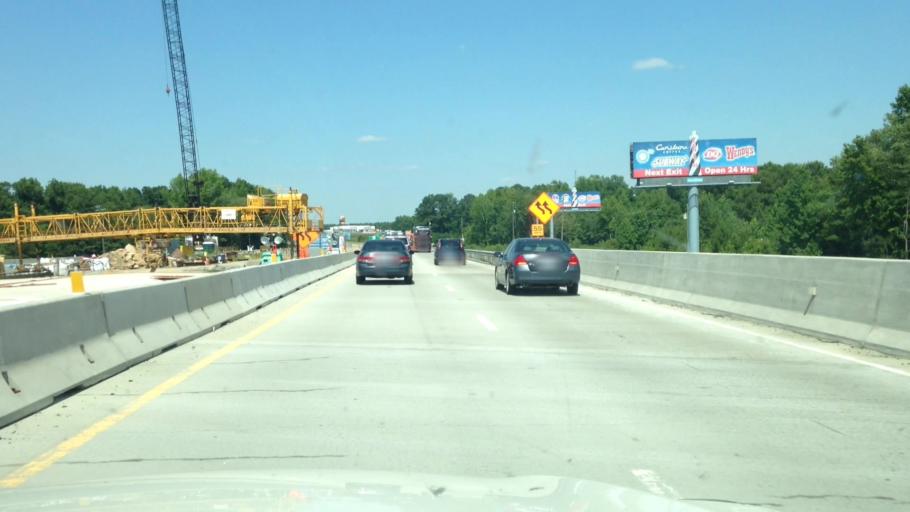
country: US
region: North Carolina
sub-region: Johnston County
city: Kenly
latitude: 35.5697
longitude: -78.1625
